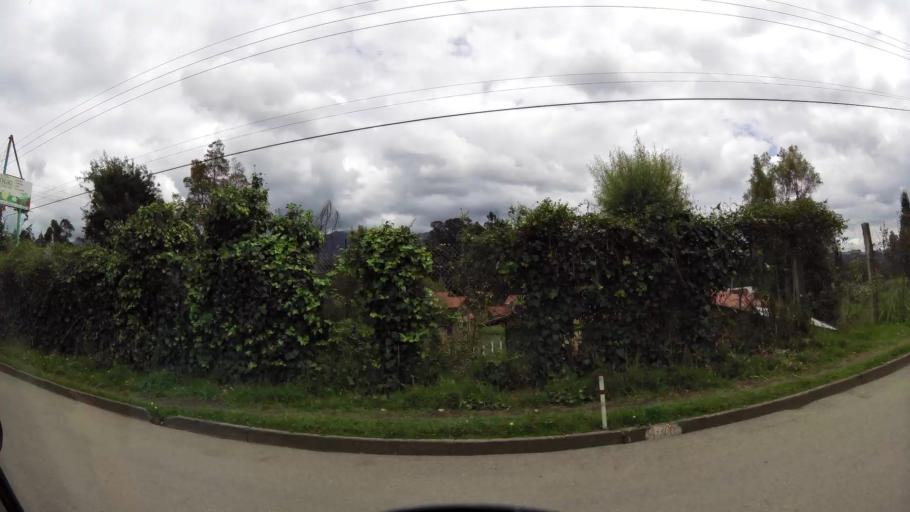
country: EC
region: Azuay
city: Cuenca
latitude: -2.8883
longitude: -79.0637
